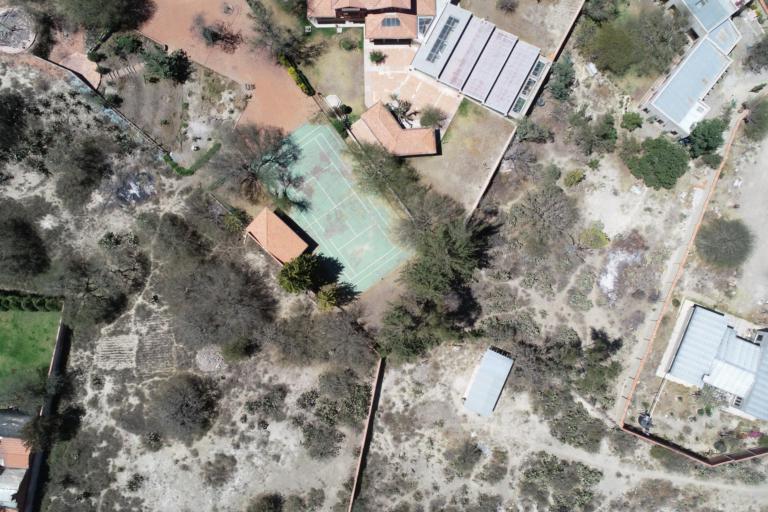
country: BO
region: La Paz
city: La Paz
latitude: -16.6307
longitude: -68.0547
